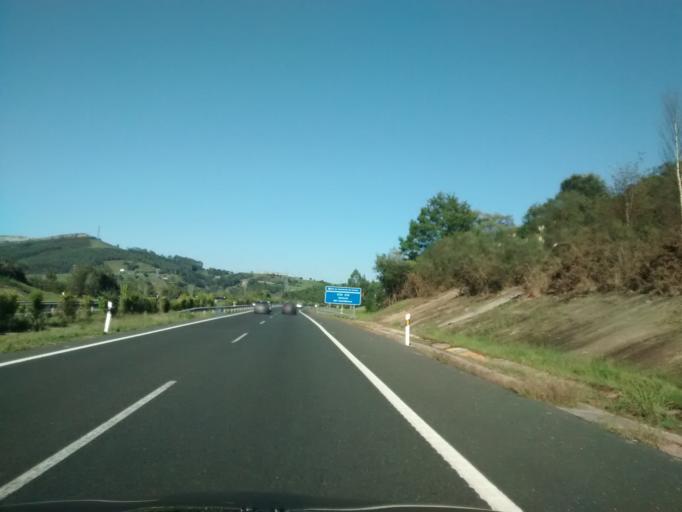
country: ES
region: Cantabria
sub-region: Provincia de Cantabria
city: Cabezon de la Sal
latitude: 43.3192
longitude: -4.2336
